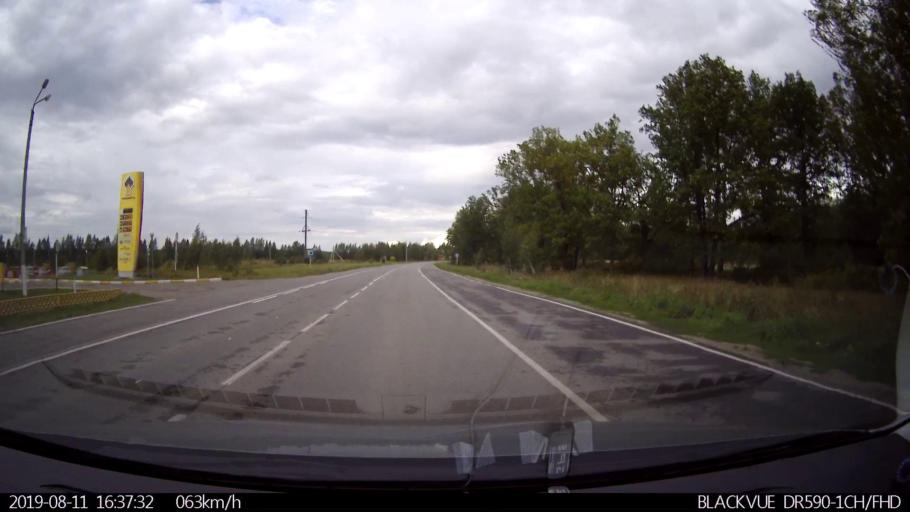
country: RU
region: Ulyanovsk
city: Mayna
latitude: 54.1282
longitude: 47.6150
